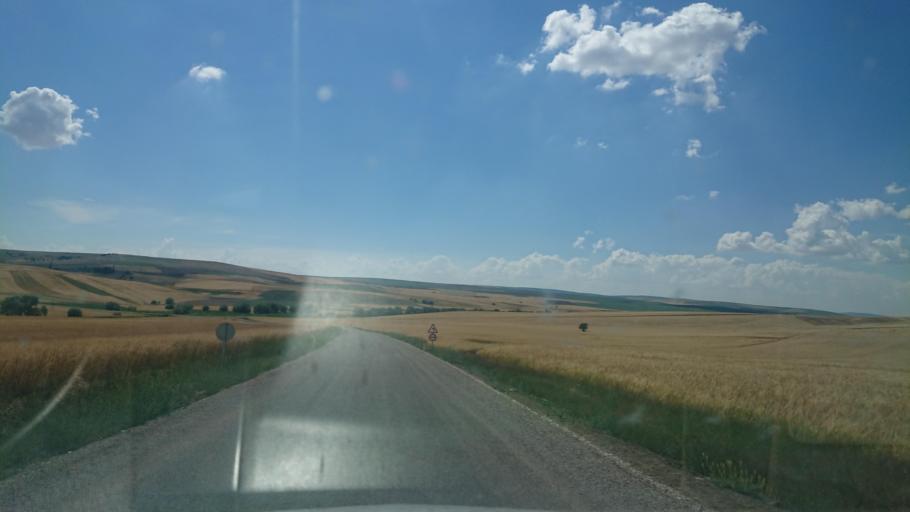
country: TR
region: Aksaray
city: Agacoren
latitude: 38.7850
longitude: 33.8021
